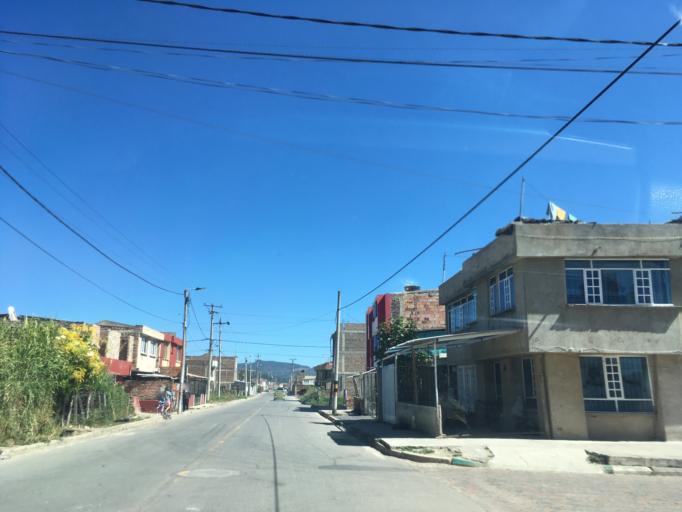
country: CO
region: Boyaca
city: Sogamoso
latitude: 5.7127
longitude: -72.9469
